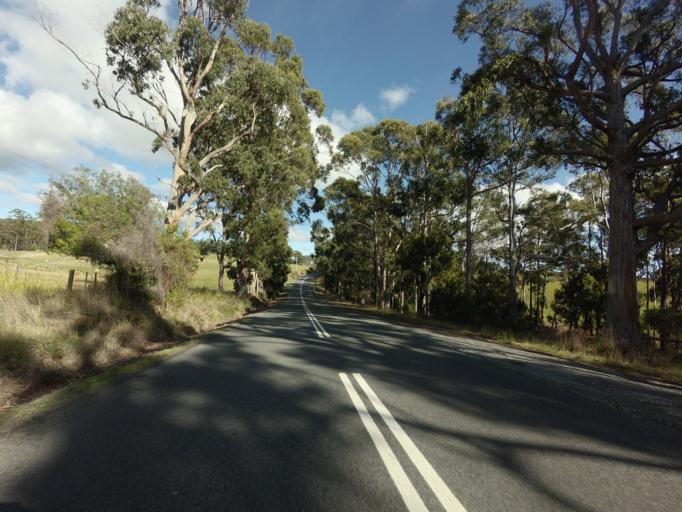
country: AU
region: Tasmania
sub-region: Clarence
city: Sandford
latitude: -43.0617
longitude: 147.8249
